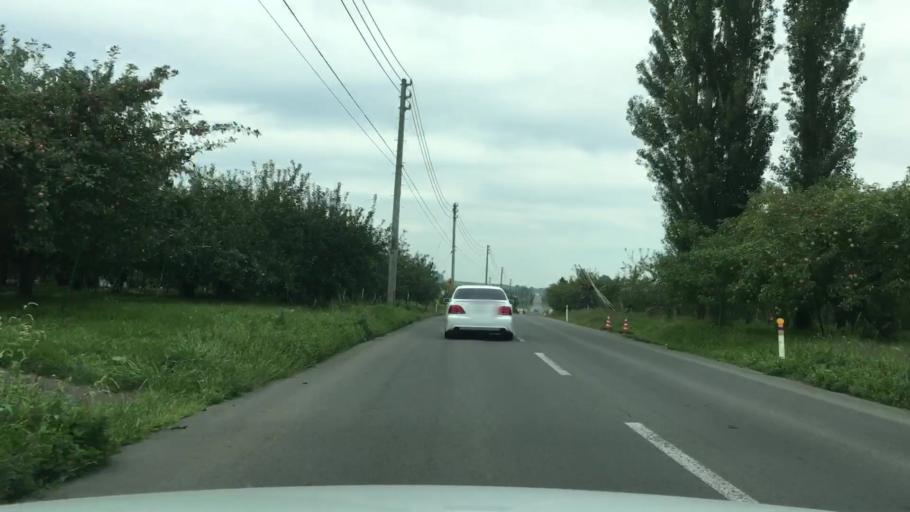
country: JP
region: Aomori
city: Hirosaki
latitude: 40.6469
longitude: 140.4237
